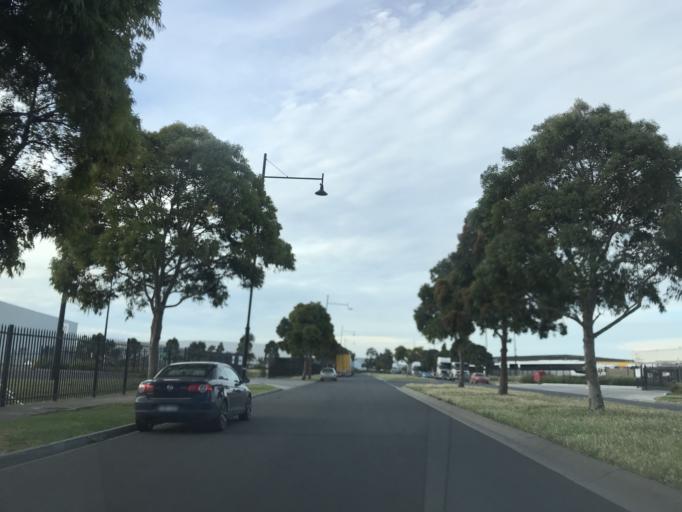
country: AU
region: Victoria
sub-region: Wyndham
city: Truganina
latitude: -37.8108
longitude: 144.7660
